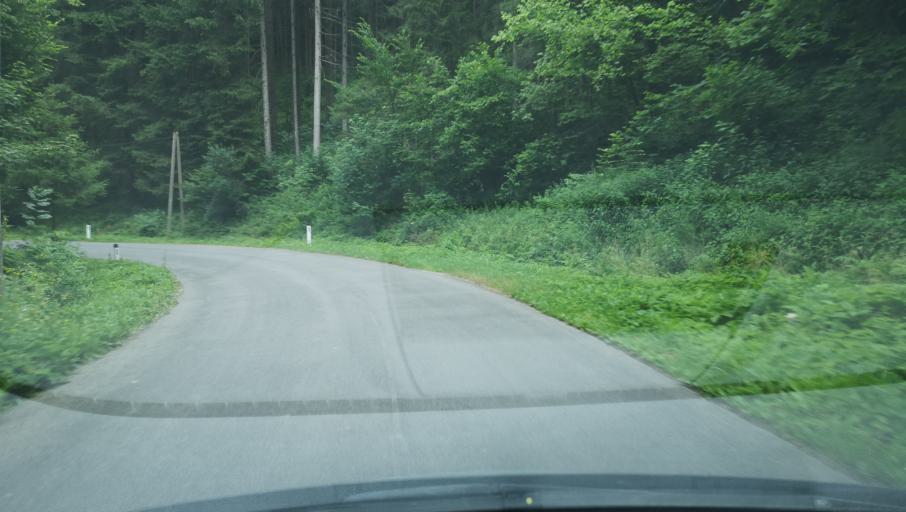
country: AT
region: Lower Austria
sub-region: Politischer Bezirk Melk
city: Nochling
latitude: 48.1817
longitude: 14.9790
